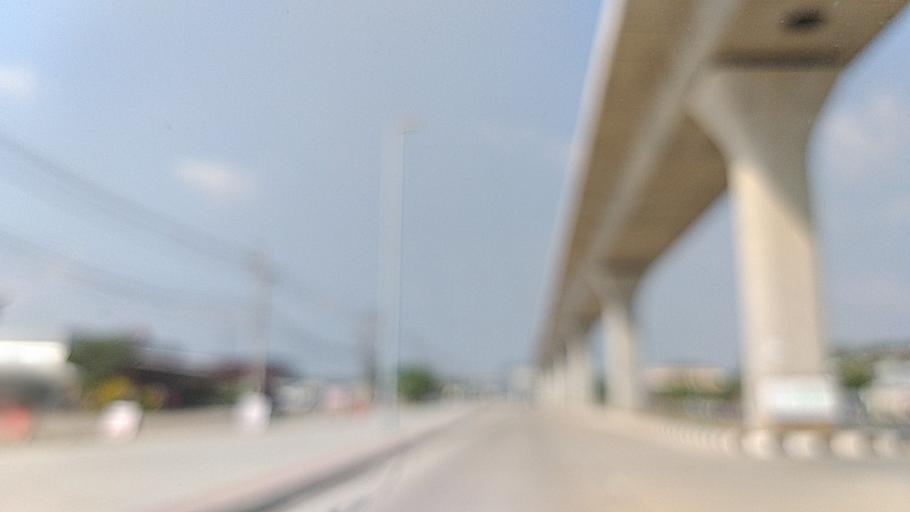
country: TH
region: Bangkok
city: Sai Mai
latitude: 13.9290
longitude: 100.6324
